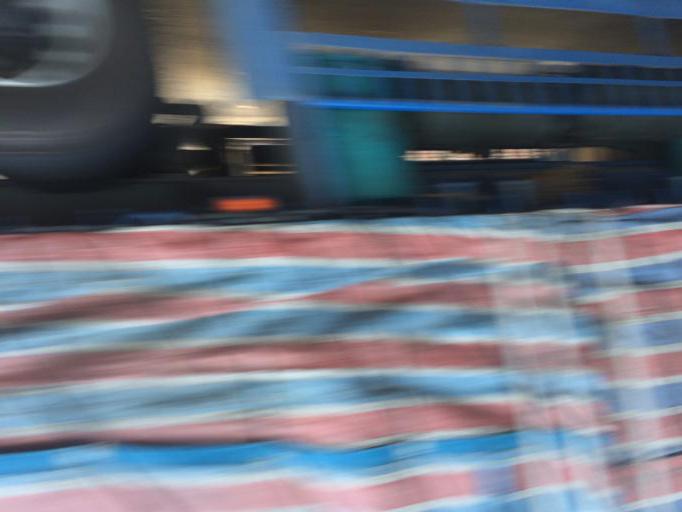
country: TW
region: Taiwan
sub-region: Hsinchu
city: Hsinchu
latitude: 24.7367
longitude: 120.9121
